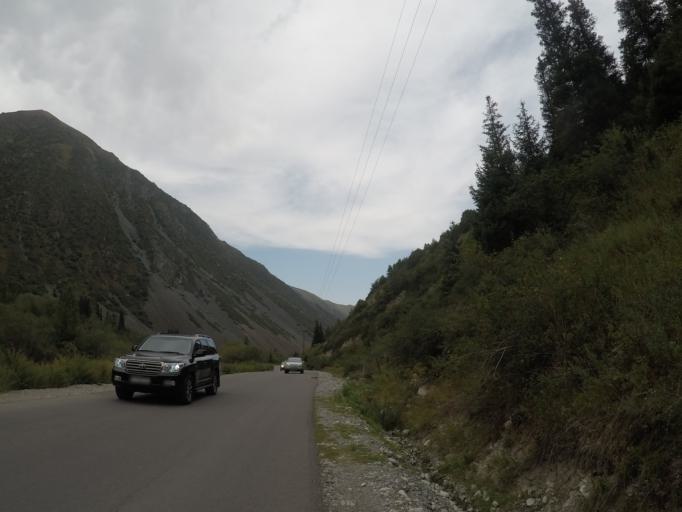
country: KG
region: Chuy
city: Bishkek
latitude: 42.5754
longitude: 74.4824
